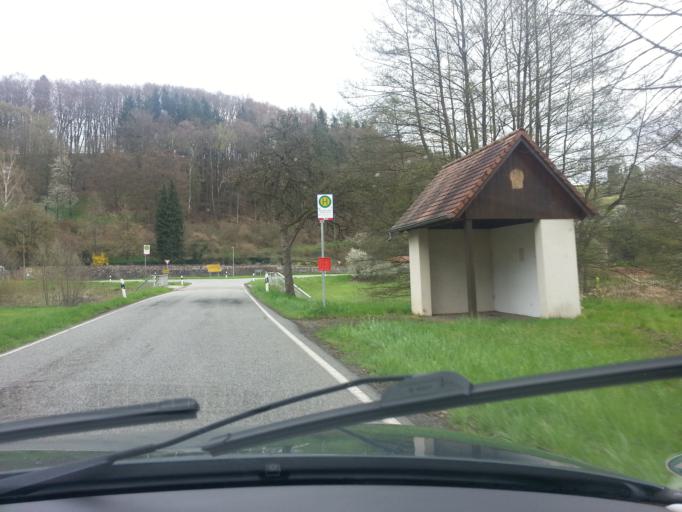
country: DE
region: Rheinland-Pfalz
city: Battweiler
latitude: 49.3016
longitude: 7.4675
